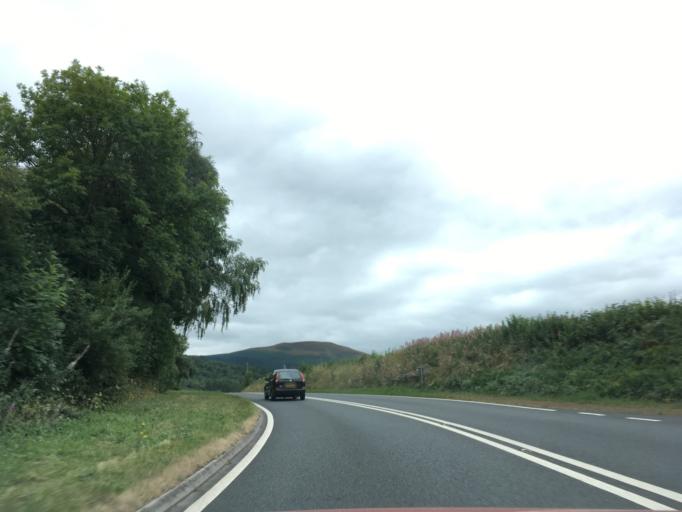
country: GB
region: Wales
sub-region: Blaenau Gwent
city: Brynmawr
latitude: 51.8945
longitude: -3.2490
